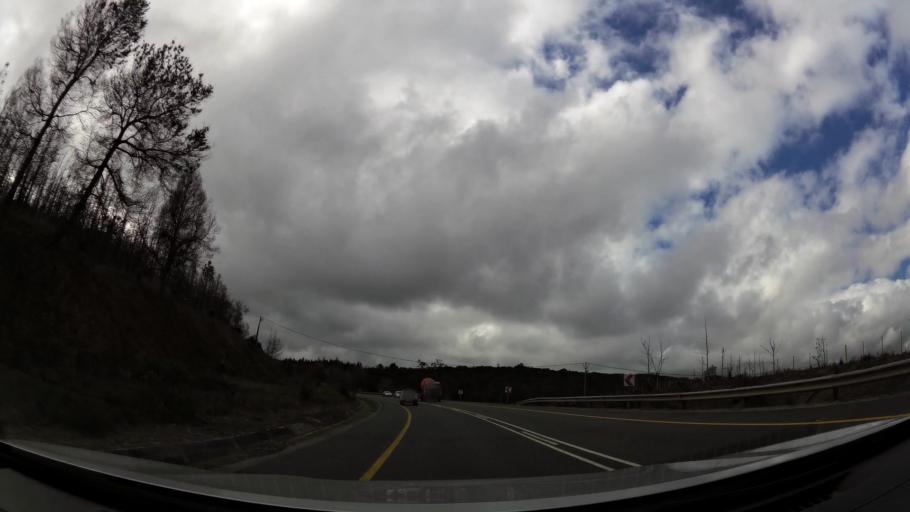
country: ZA
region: Western Cape
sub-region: Eden District Municipality
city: Knysna
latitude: -34.0350
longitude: 23.1578
